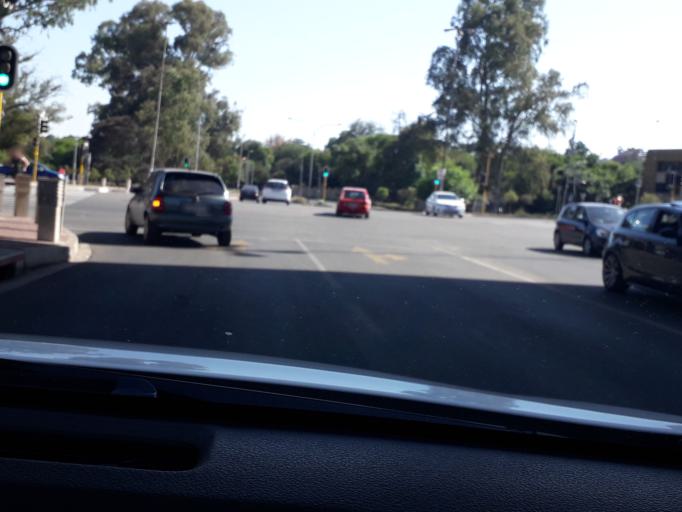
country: ZA
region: Gauteng
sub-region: City of Johannesburg Metropolitan Municipality
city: Johannesburg
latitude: -26.1837
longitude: 28.0206
